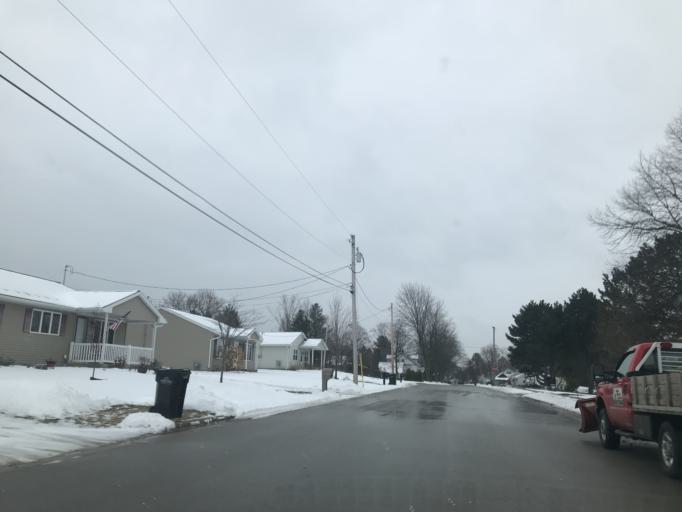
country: US
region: Wisconsin
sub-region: Door County
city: Sturgeon Bay
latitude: 44.8439
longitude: -87.3743
